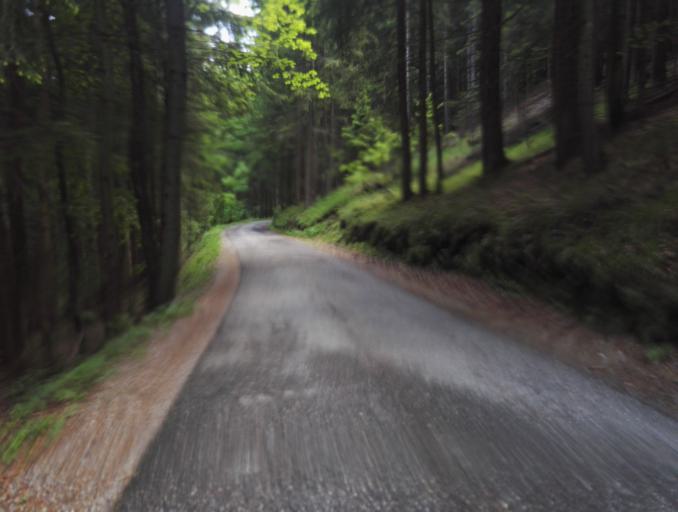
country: AT
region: Styria
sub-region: Politischer Bezirk Graz-Umgebung
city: Semriach
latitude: 47.1975
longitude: 15.4392
